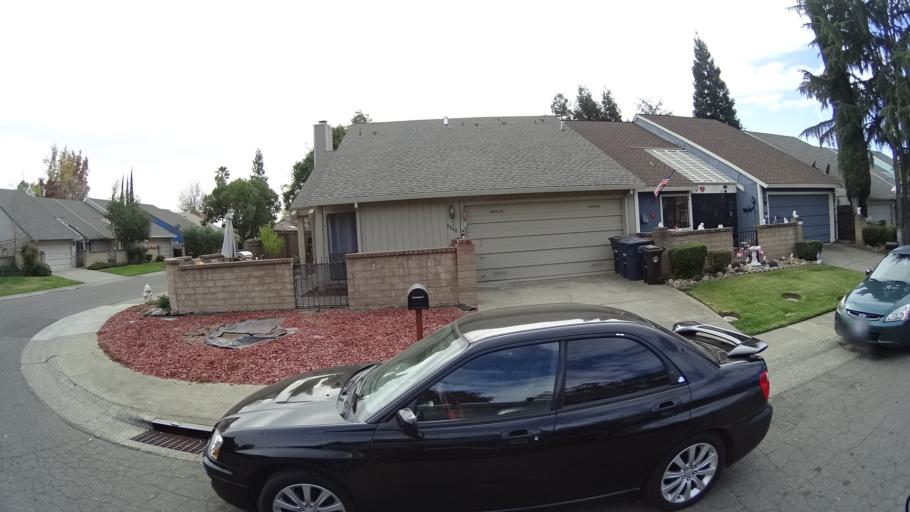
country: US
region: California
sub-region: Sacramento County
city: Fair Oaks
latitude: 38.6709
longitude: -121.2655
